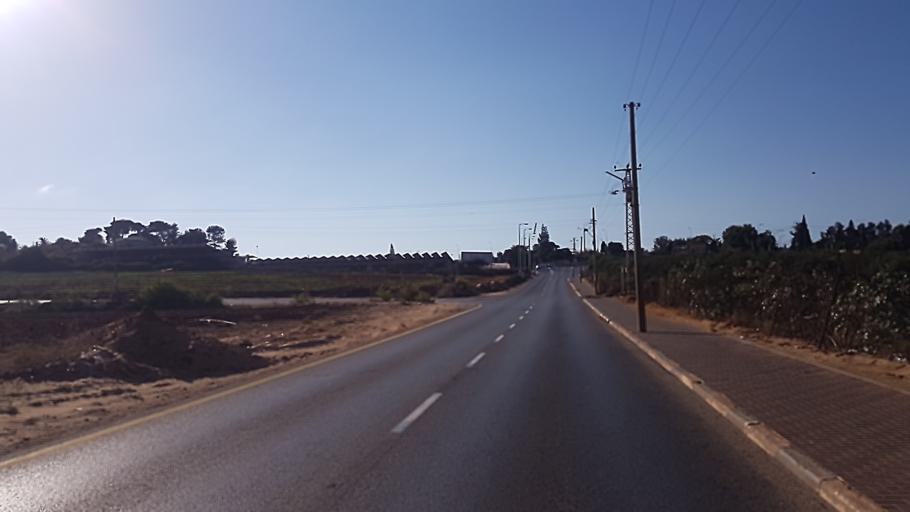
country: IL
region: Central District
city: Kfar Saba
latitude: 32.1985
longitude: 34.9192
